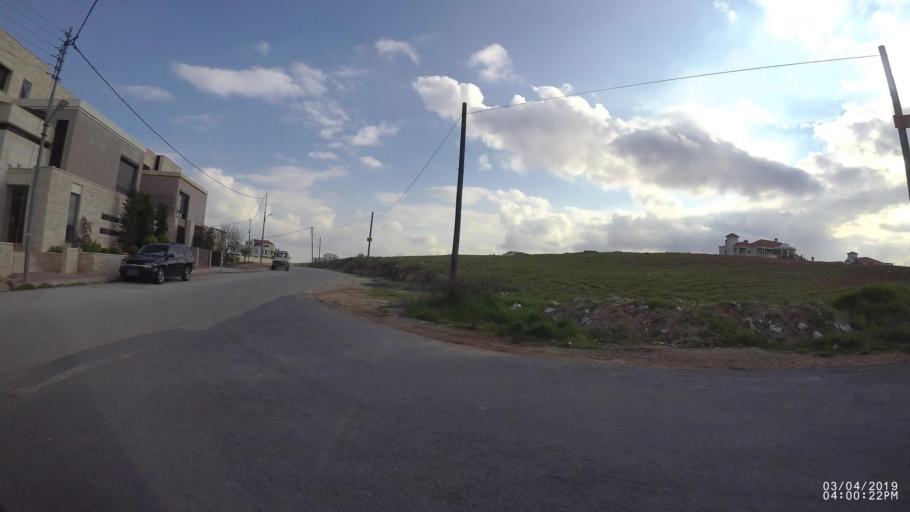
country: JO
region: Amman
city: Al Bunayyat ash Shamaliyah
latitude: 31.9119
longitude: 35.8759
